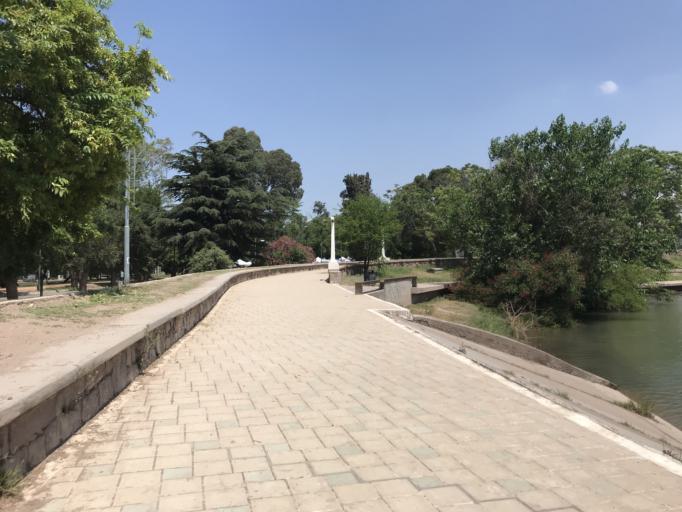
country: AR
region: Mendoza
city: Mendoza
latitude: -32.8973
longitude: -68.8642
